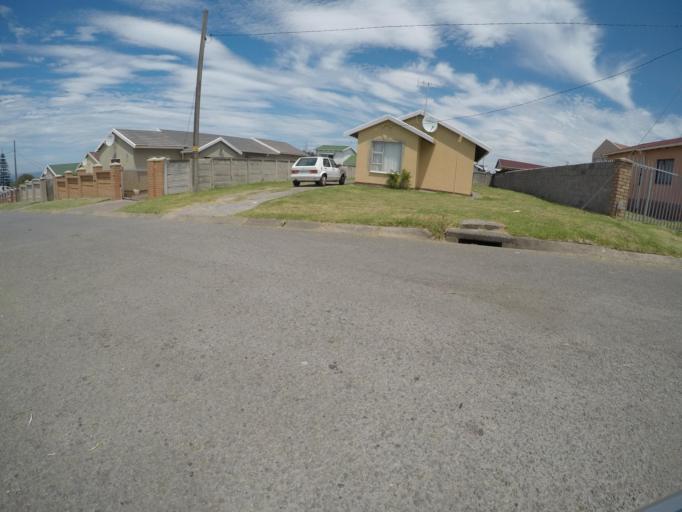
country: ZA
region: Eastern Cape
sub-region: Buffalo City Metropolitan Municipality
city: East London
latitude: -33.0416
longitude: 27.8644
